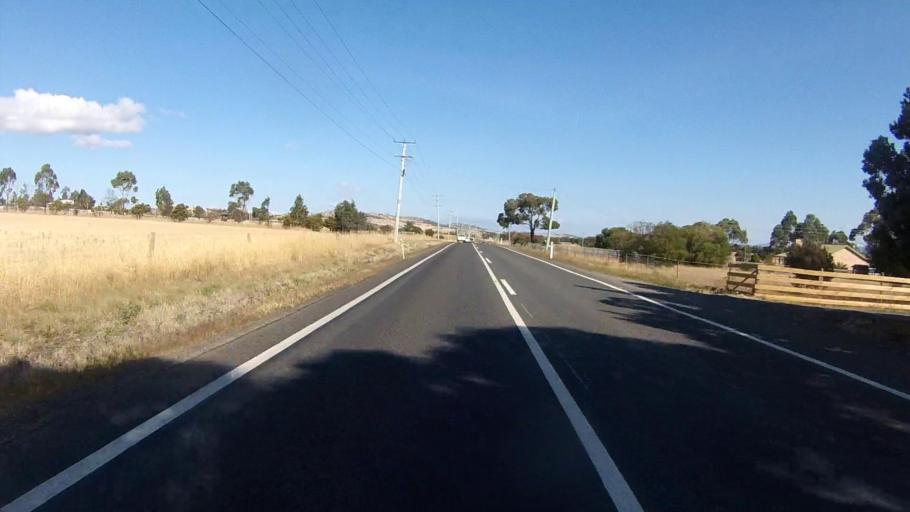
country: AU
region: Tasmania
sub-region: Sorell
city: Sorell
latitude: -42.7341
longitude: 147.5290
